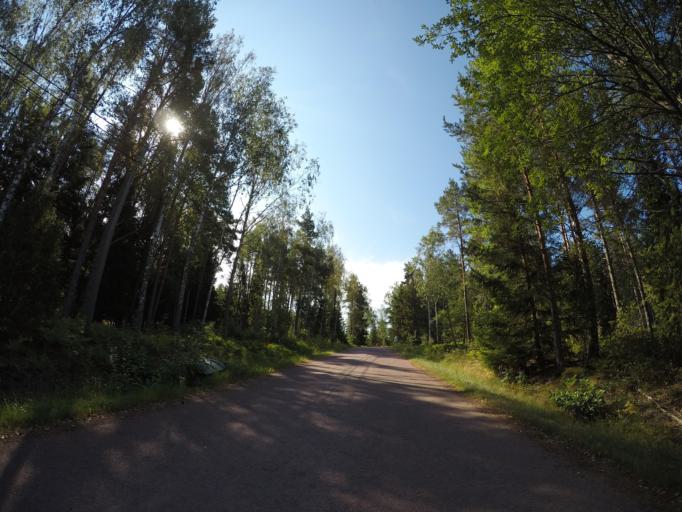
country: AX
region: Alands landsbygd
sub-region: Finstroem
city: Finstroem
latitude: 60.2811
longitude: 19.9169
